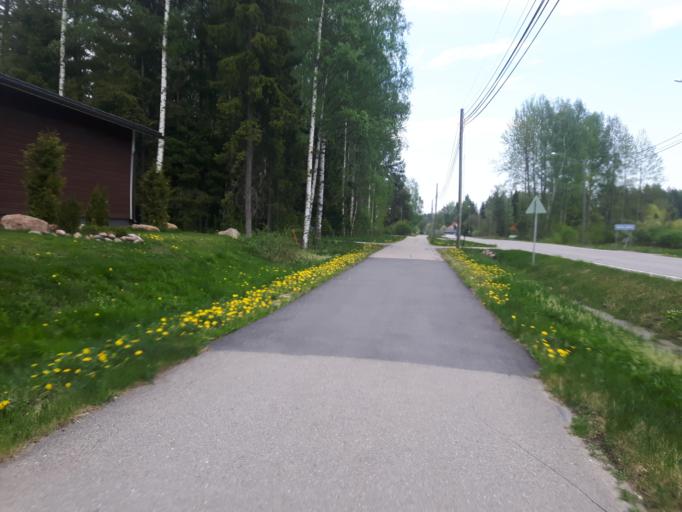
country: FI
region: Uusimaa
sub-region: Porvoo
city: Porvoo
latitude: 60.4014
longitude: 25.7059
